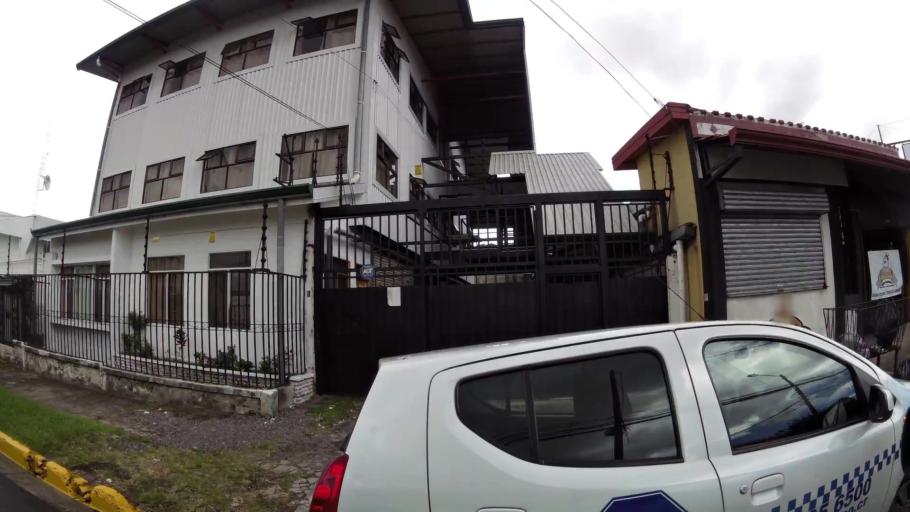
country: CR
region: San Jose
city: San Pedro
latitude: 9.9293
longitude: -84.0482
